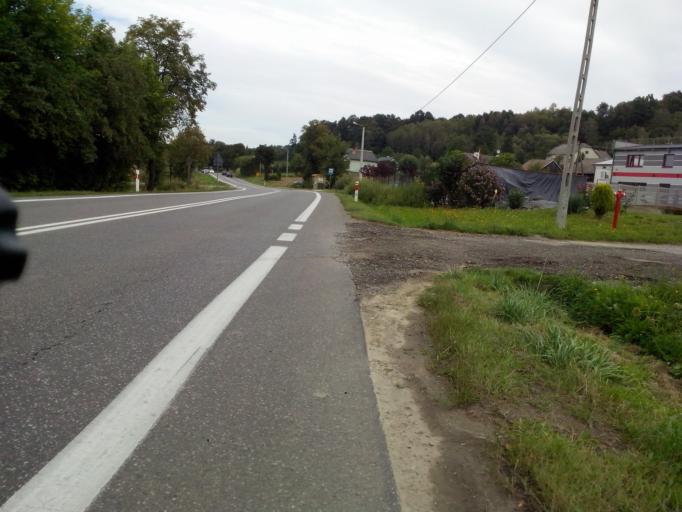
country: PL
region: Subcarpathian Voivodeship
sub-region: Powiat brzozowski
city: Domaradz
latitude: 49.7686
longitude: 21.9545
